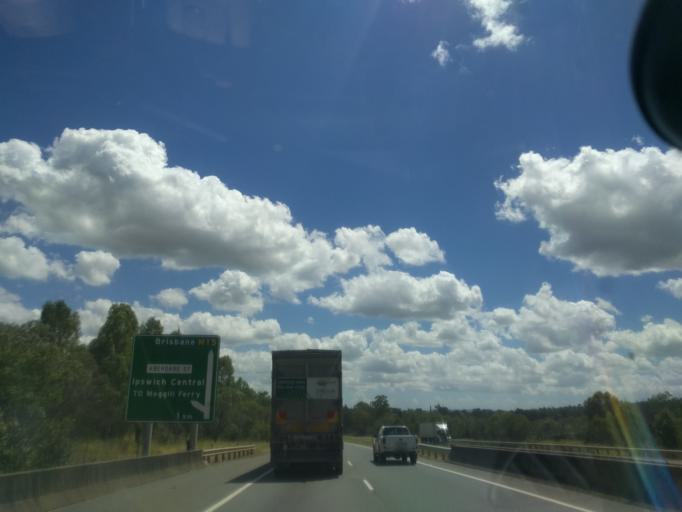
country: AU
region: Queensland
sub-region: Ipswich
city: Bundamba
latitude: -27.6097
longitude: 152.8286
